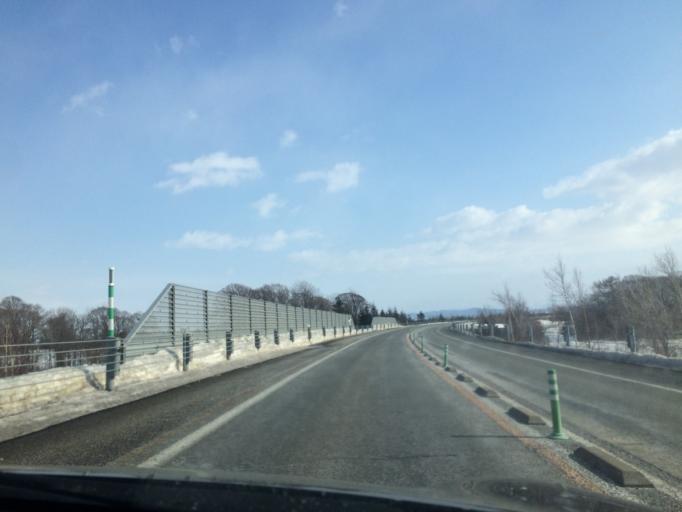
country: JP
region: Hokkaido
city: Chitose
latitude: 42.8821
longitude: 141.6212
